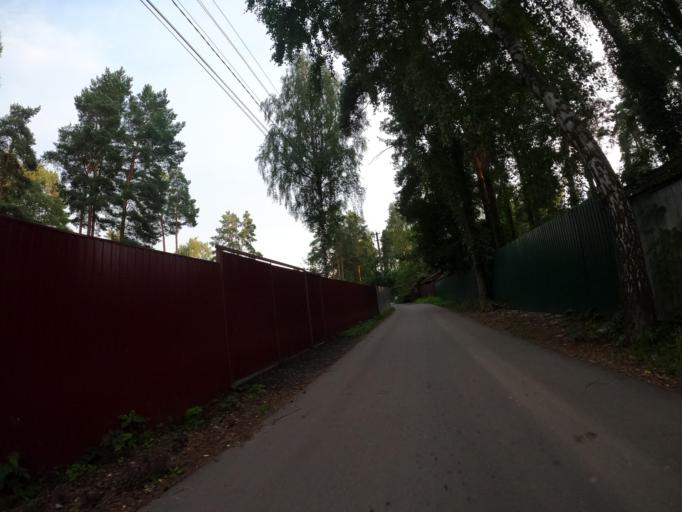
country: RU
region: Moskovskaya
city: Bykovo
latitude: 55.6411
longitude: 38.0819
